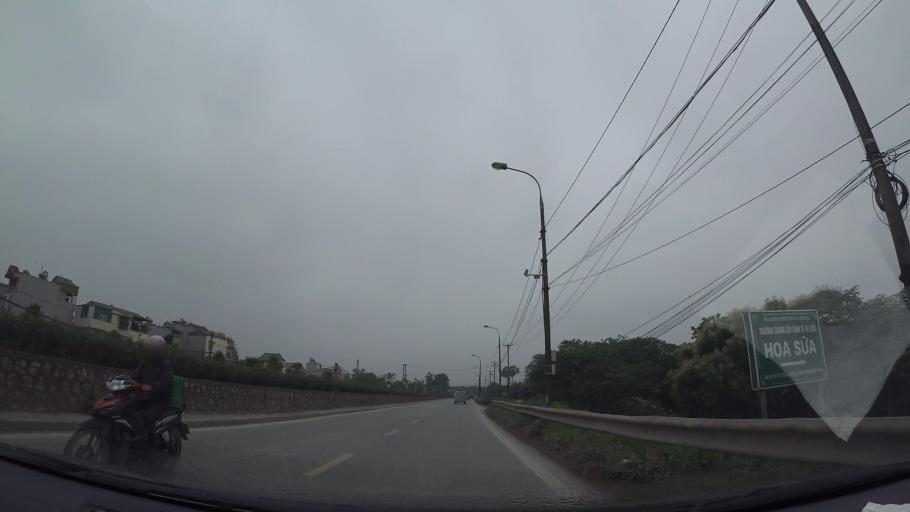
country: VN
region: Ha Noi
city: Hai BaTrung
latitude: 20.9898
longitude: 105.8937
